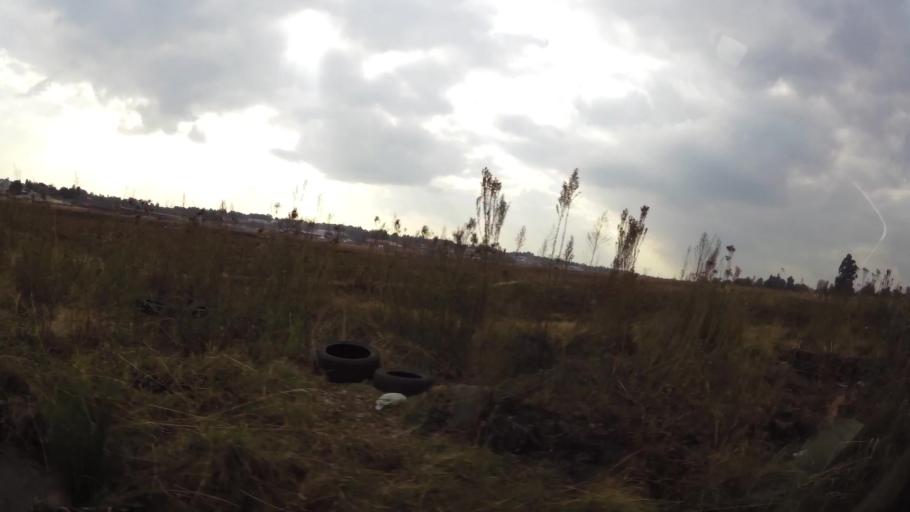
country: ZA
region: Gauteng
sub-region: Ekurhuleni Metropolitan Municipality
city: Benoni
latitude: -26.1376
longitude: 28.3570
